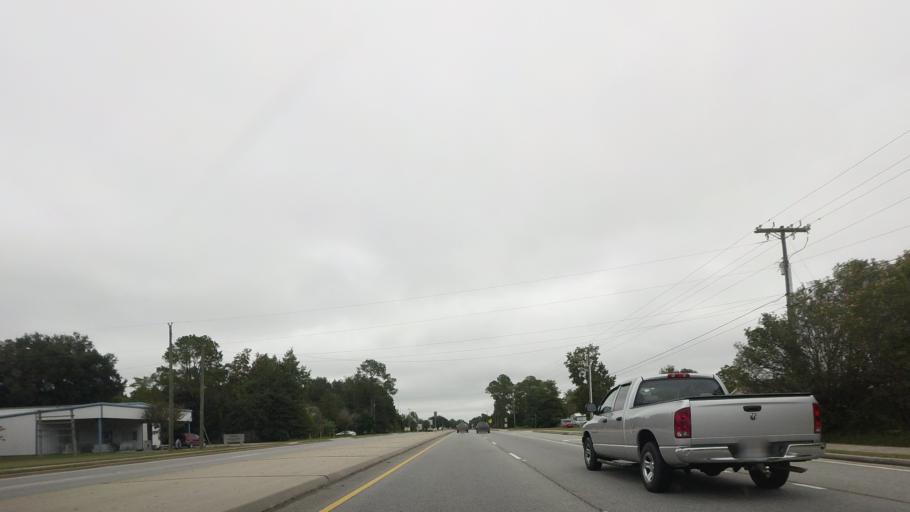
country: US
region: Georgia
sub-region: Lowndes County
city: Valdosta
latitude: 30.9248
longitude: -83.2489
